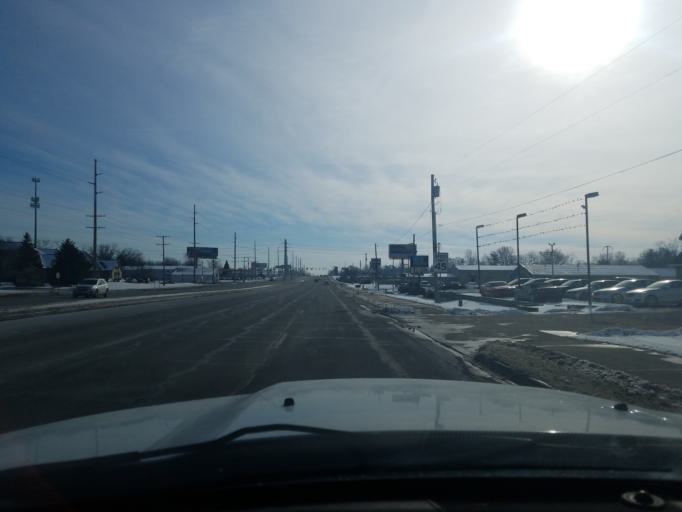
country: US
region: Indiana
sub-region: Allen County
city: Fort Wayne
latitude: 41.1702
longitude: -85.1660
